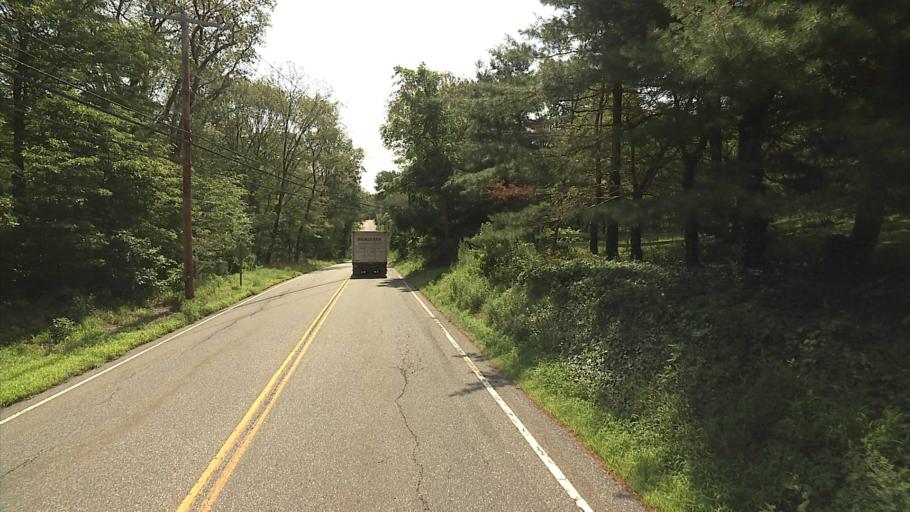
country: US
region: Connecticut
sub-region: New London County
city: Montville Center
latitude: 41.5027
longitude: -72.2353
